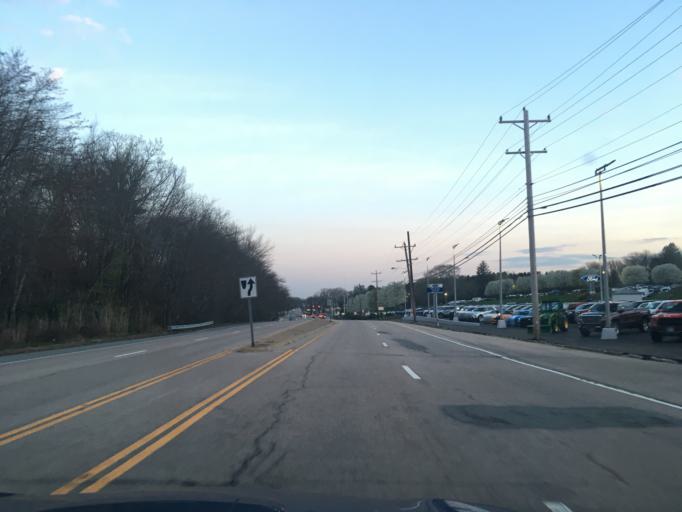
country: US
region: Rhode Island
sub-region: Kent County
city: East Greenwich
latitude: 41.6305
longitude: -71.4933
